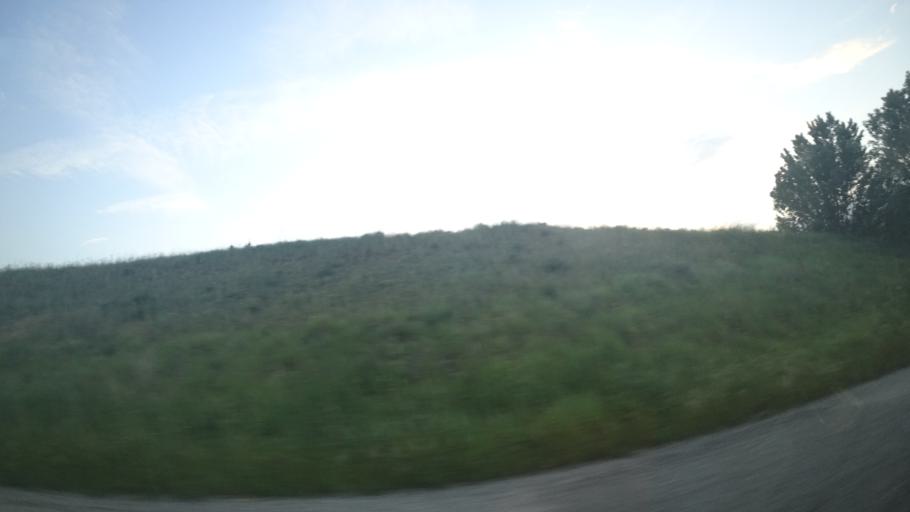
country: FR
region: Languedoc-Roussillon
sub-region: Departement de l'Herault
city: Maraussan
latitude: 43.3475
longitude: 3.1727
